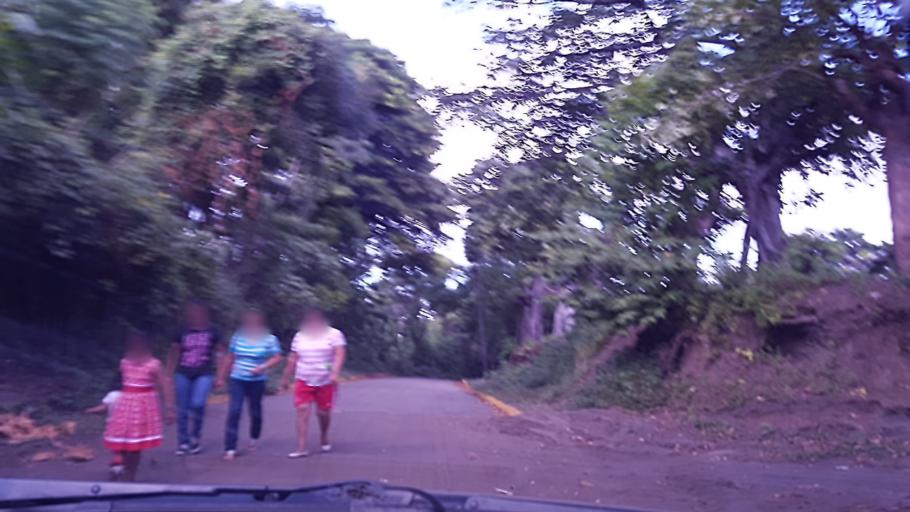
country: NI
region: Masaya
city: Ticuantepe
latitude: 11.9923
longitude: -86.2247
